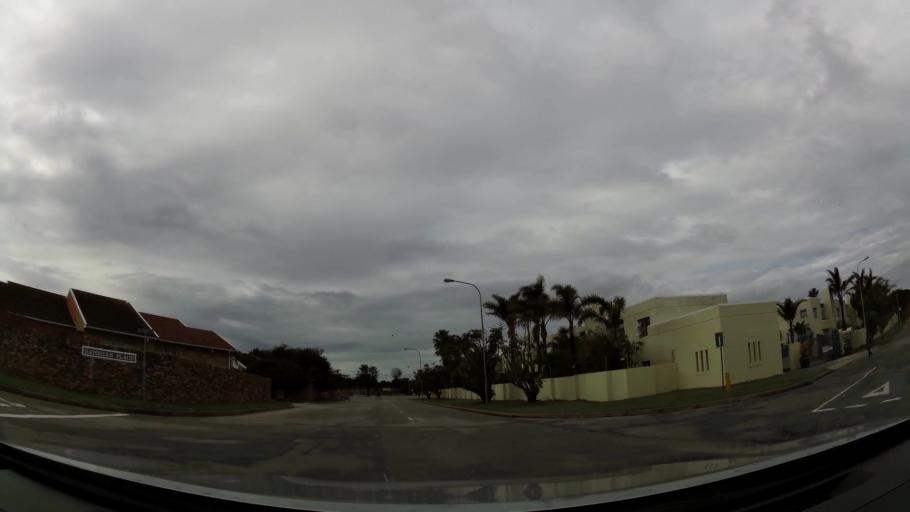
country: ZA
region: Eastern Cape
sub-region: Nelson Mandela Bay Metropolitan Municipality
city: Port Elizabeth
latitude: -33.9723
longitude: 25.6207
